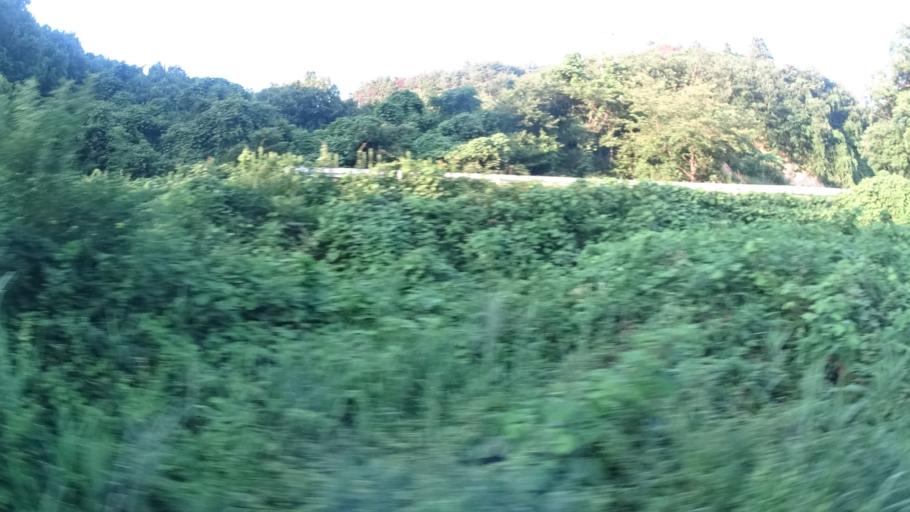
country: JP
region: Fukushima
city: Miharu
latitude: 37.4554
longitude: 140.5147
